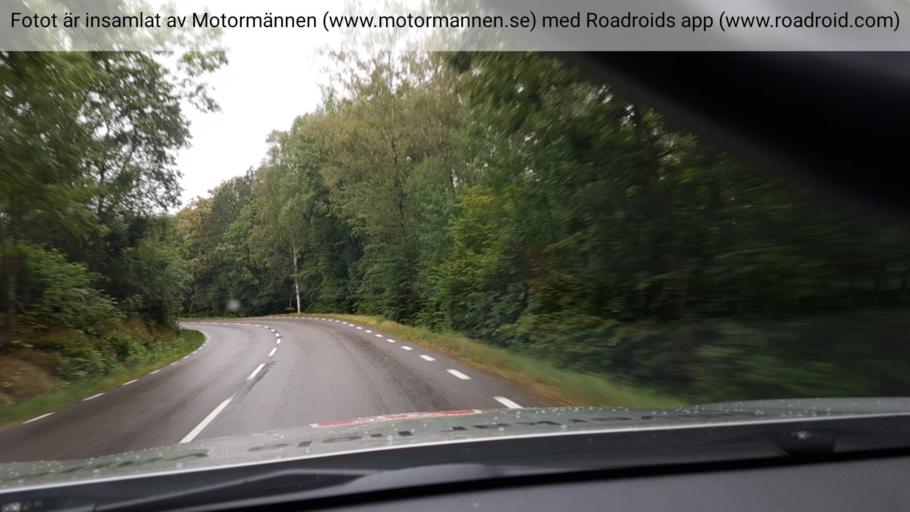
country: SE
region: Vaestra Goetaland
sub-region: Alingsas Kommun
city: Alingsas
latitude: 57.8603
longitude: 12.5615
